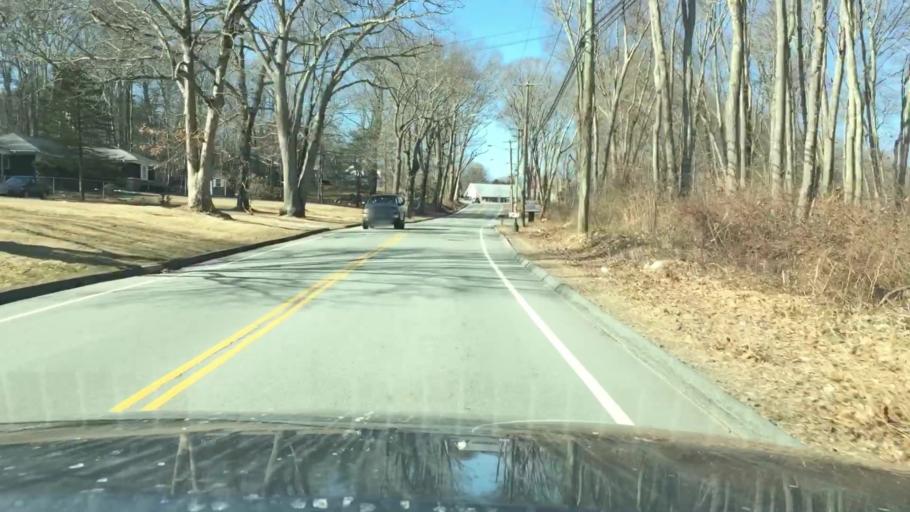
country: US
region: Connecticut
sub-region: New London County
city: Conning Towers-Nautilus Park
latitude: 41.3720
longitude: -72.0647
